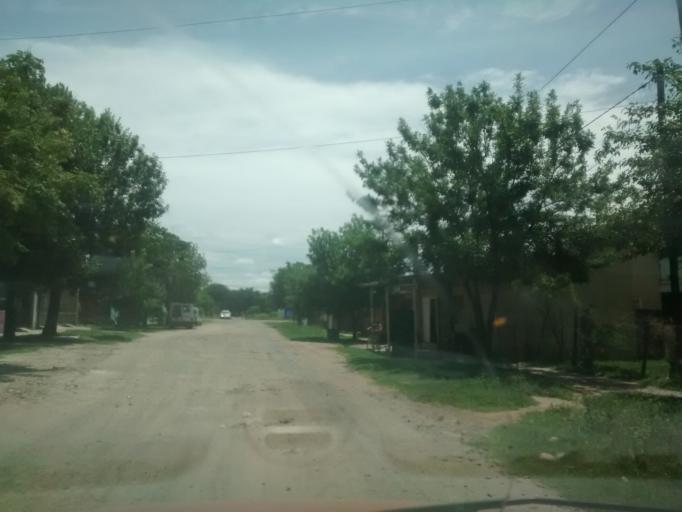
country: AR
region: Chaco
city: Resistencia
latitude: -27.4362
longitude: -58.9761
